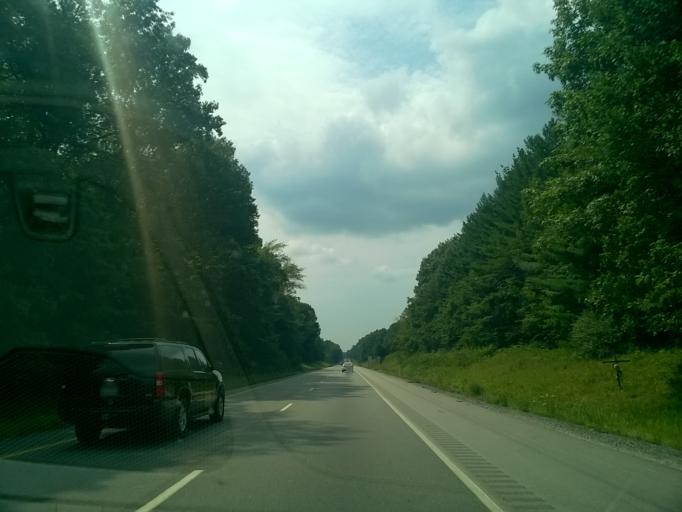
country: US
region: Indiana
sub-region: Putnam County
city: Cloverdale
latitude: 39.5237
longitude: -86.8912
